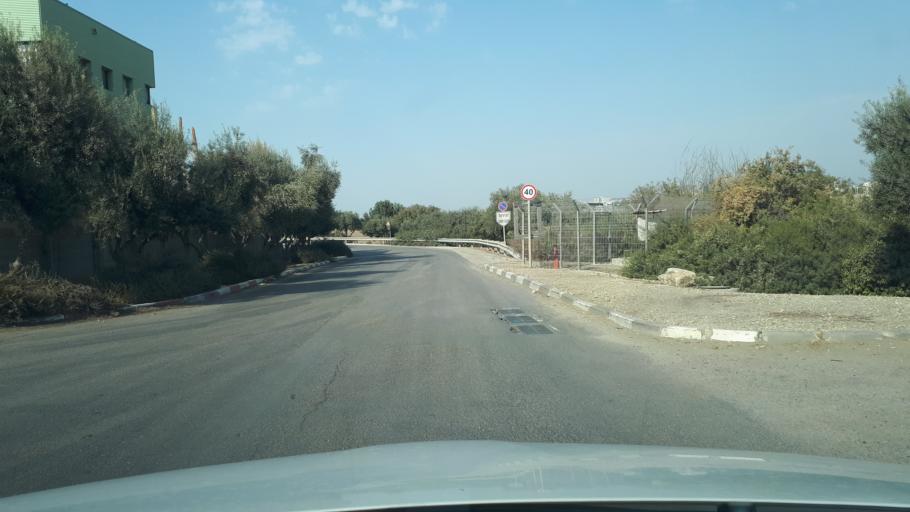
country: IL
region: Central District
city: Rosh Ha'Ayin
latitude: 32.0842
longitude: 34.9439
